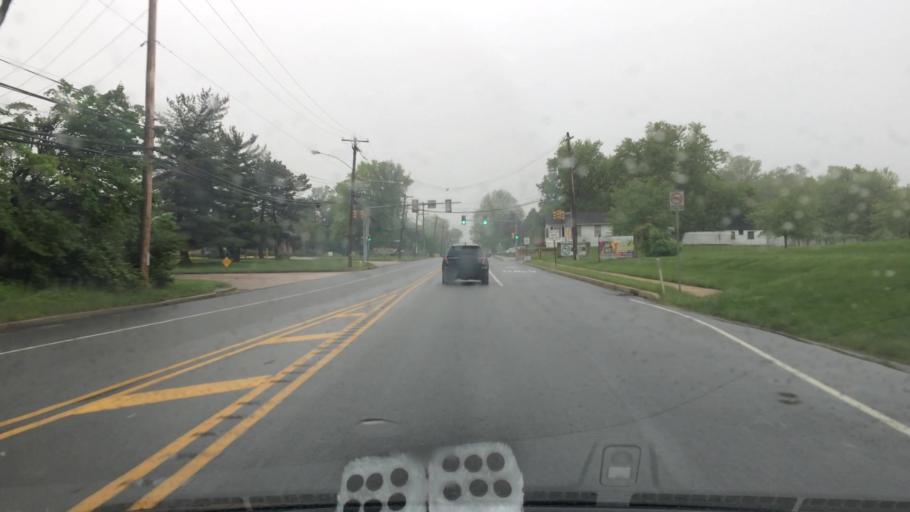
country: US
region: Pennsylvania
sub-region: Delaware County
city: Village Green-Green Ridge
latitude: 39.8520
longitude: -75.4264
